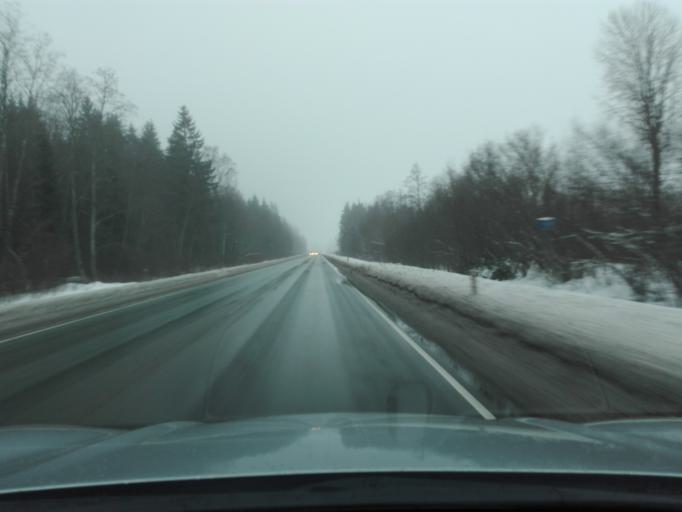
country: EE
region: Raplamaa
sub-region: Kohila vald
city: Kohila
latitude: 59.2395
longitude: 24.7591
